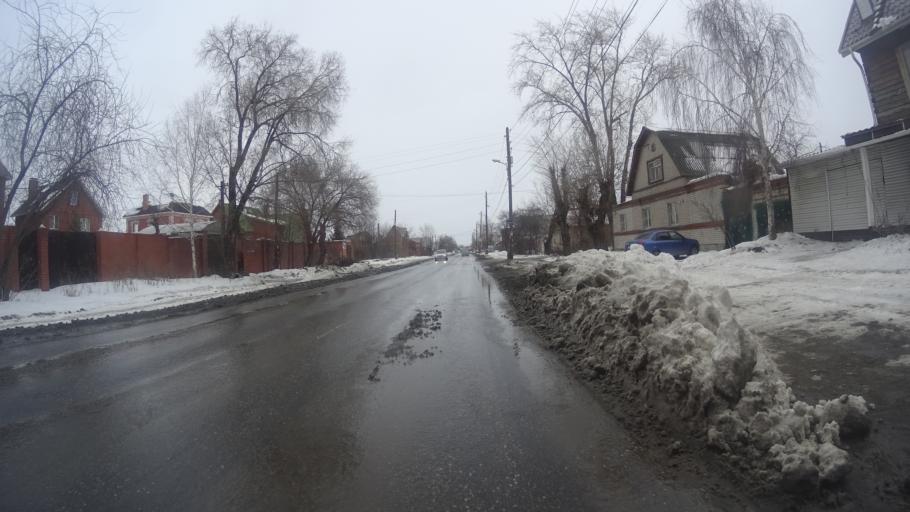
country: RU
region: Chelyabinsk
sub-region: Gorod Chelyabinsk
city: Chelyabinsk
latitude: 55.1338
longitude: 61.3808
